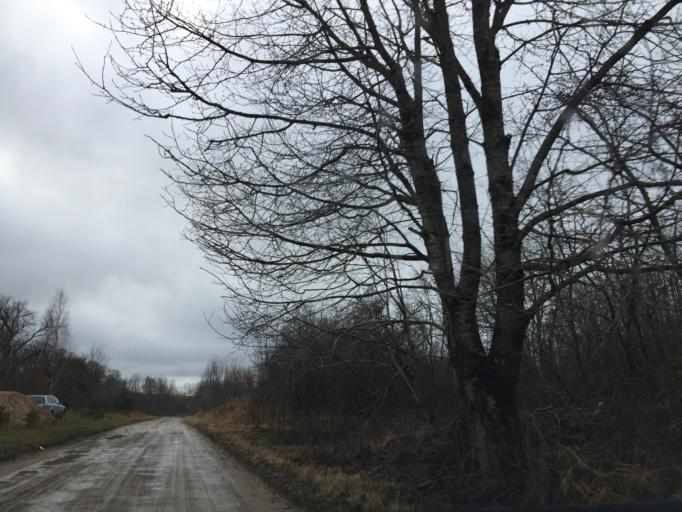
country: LV
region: Broceni
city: Broceni
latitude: 56.6666
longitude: 22.5530
